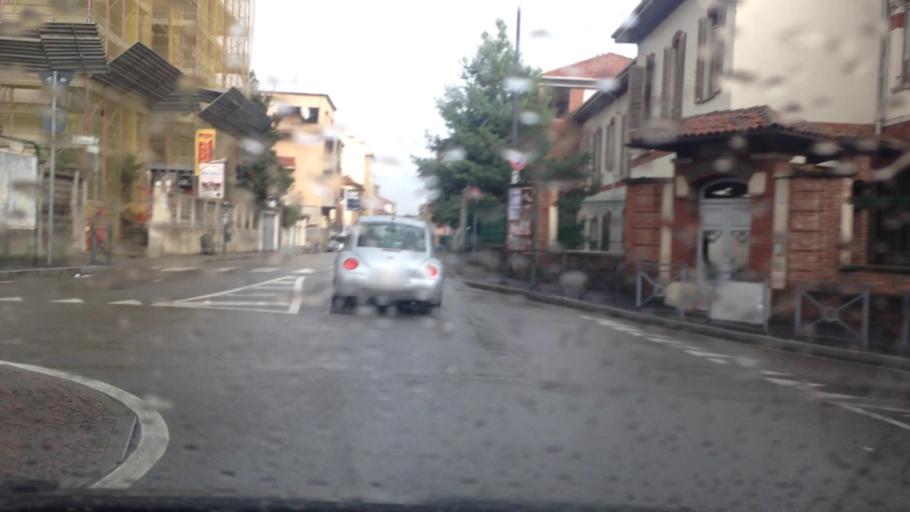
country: IT
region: Piedmont
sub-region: Provincia di Asti
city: Asti
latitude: 44.9046
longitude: 8.2110
